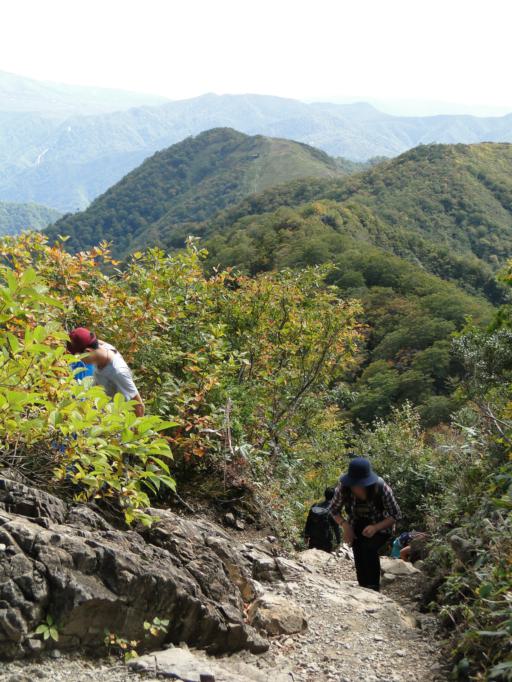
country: JP
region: Gunma
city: Numata
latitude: 36.8244
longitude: 138.9349
